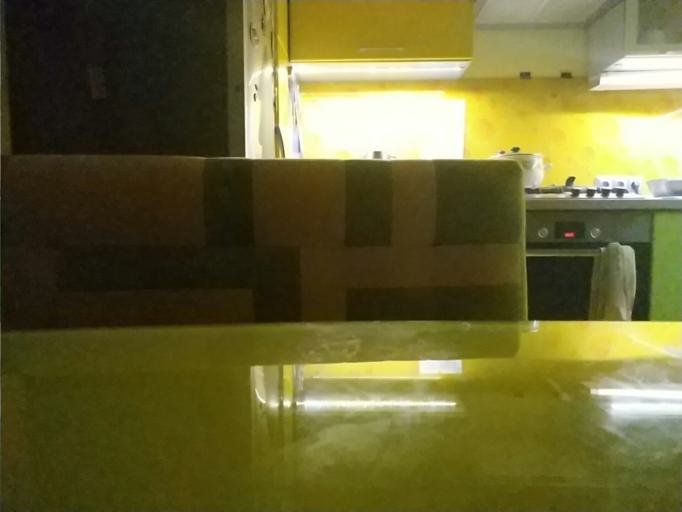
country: RU
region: Republic of Karelia
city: Pyaozerskiy
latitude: 65.4292
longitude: 30.6424
